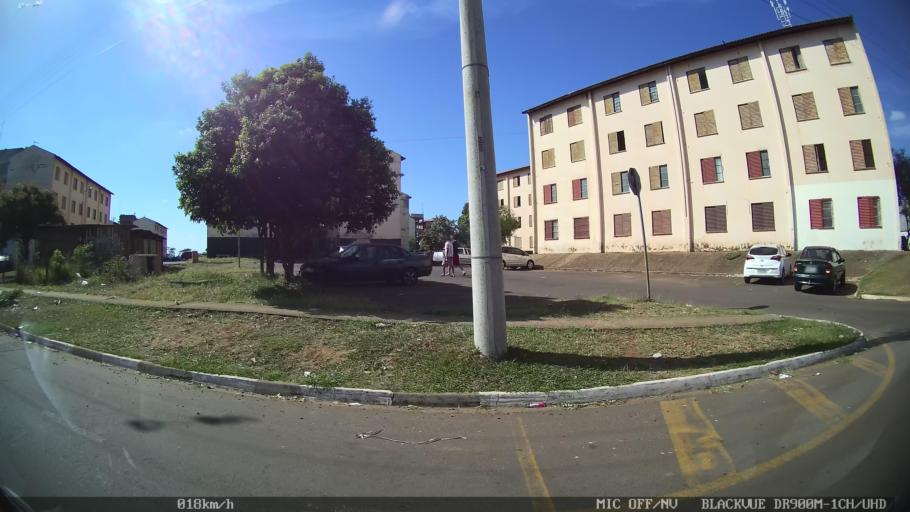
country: BR
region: Sao Paulo
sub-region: Franca
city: Franca
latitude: -20.4810
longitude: -47.4029
